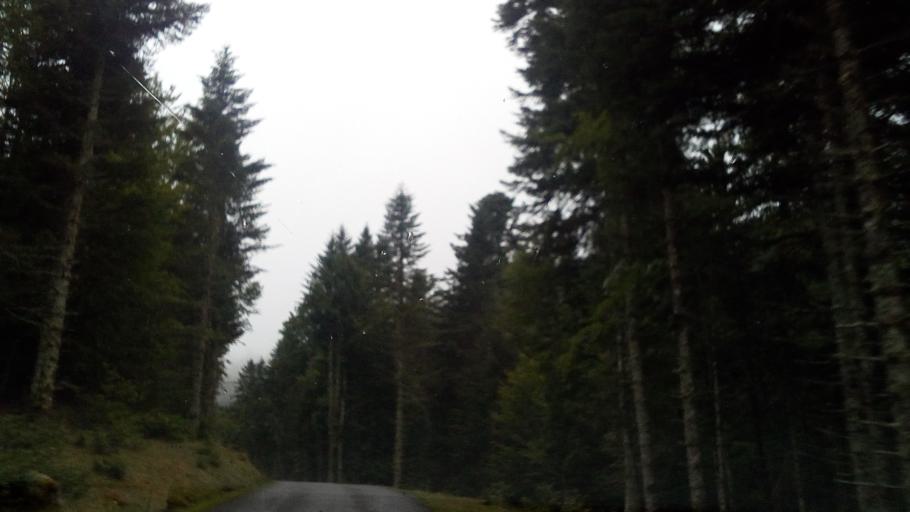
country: FR
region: Midi-Pyrenees
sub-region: Departement des Hautes-Pyrenees
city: Saint-Lary-Soulan
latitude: 42.9232
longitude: 0.2891
